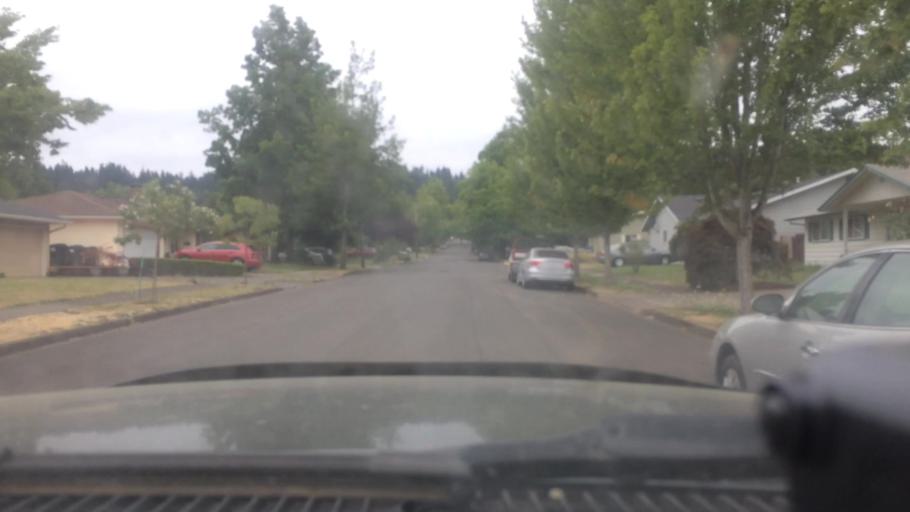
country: US
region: Oregon
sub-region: Lane County
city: Eugene
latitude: 44.0322
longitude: -123.1132
